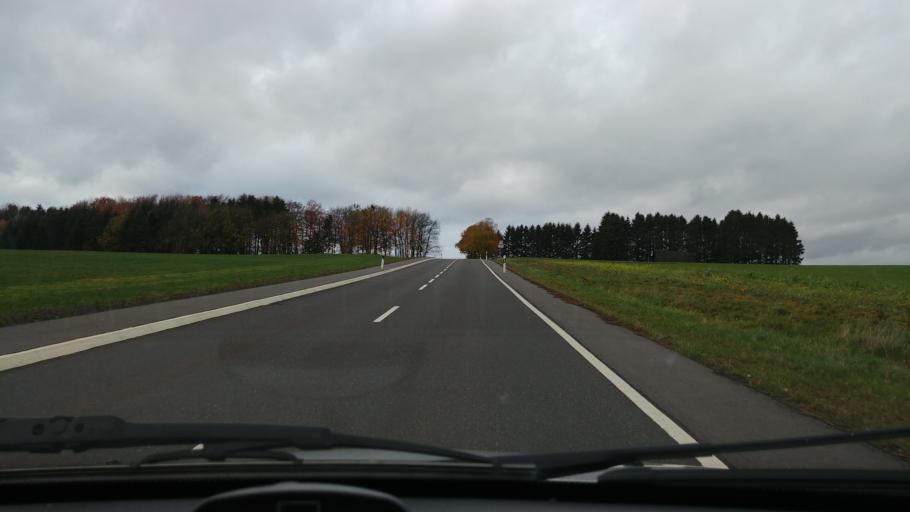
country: DE
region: Rheinland-Pfalz
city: Stockhausen-Illfurth
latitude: 50.6473
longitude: 7.9820
